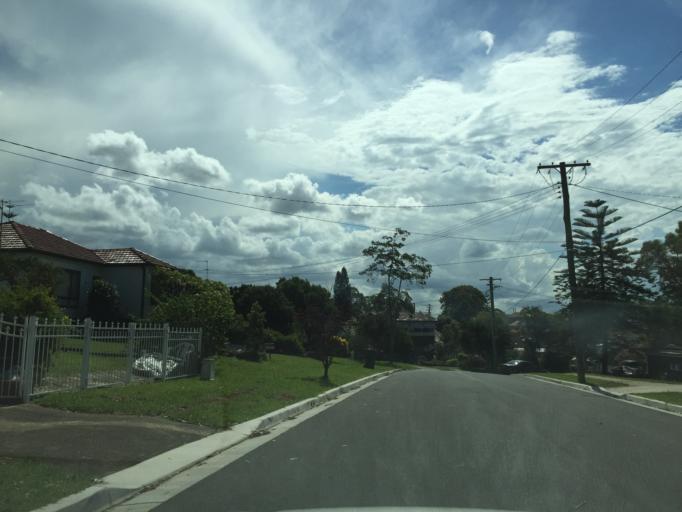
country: AU
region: New South Wales
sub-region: Blacktown
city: Doonside
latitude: -33.7783
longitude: 150.8905
